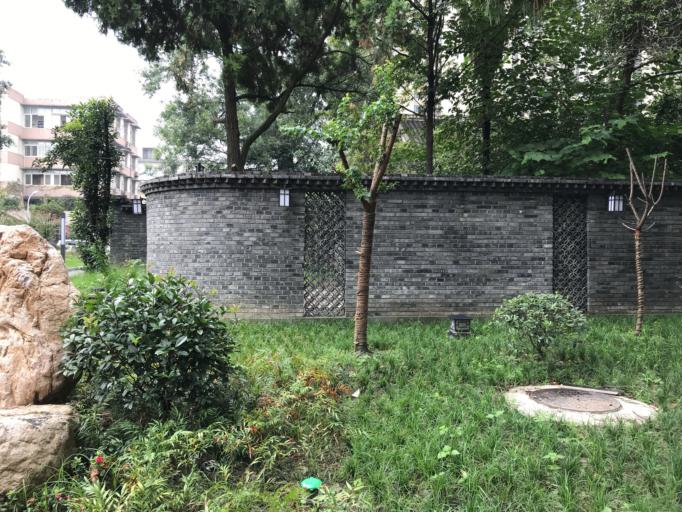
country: CN
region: Sichuan
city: Chengdu
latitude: 30.6368
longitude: 104.0879
